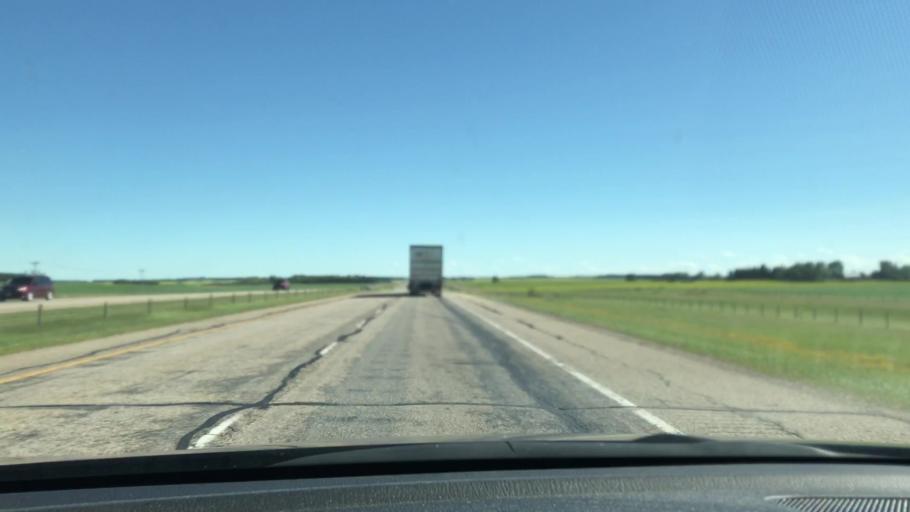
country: CA
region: Alberta
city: Olds
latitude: 51.8740
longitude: -114.0256
